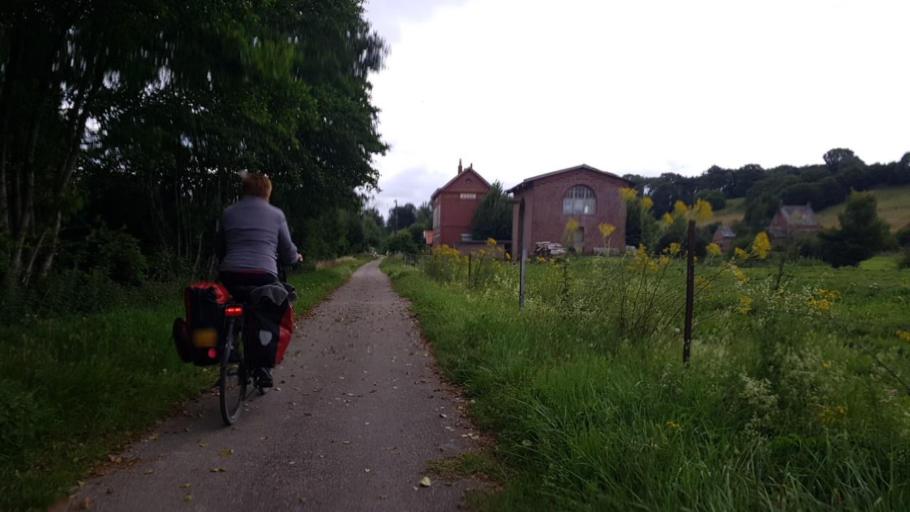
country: FR
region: Picardie
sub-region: Departement de l'Aisne
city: Buironfosse
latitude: 49.9026
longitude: 3.8236
